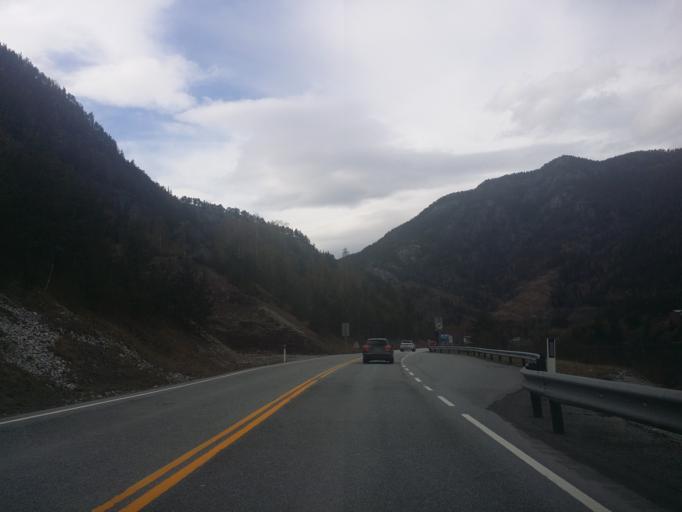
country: NO
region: Buskerud
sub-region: Nes
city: Nesbyen
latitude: 60.4776
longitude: 9.2252
